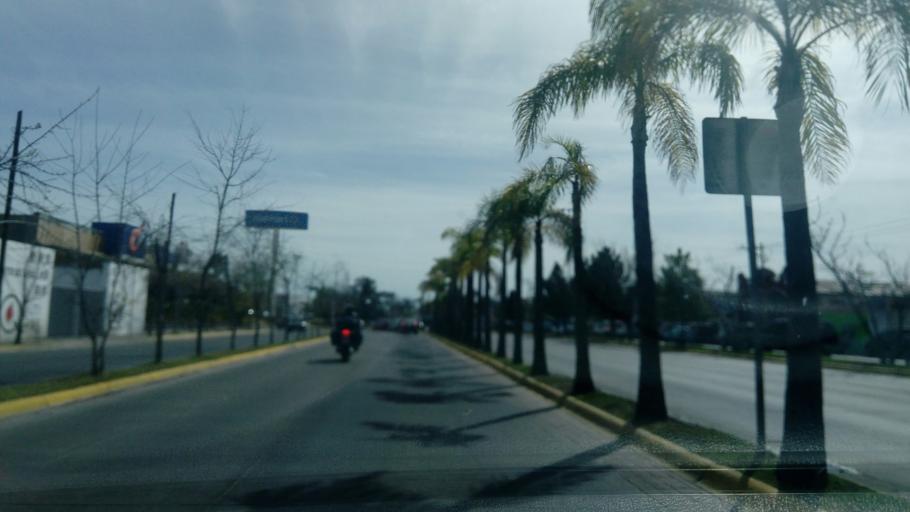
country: MX
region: Durango
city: Victoria de Durango
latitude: 24.0040
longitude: -104.6545
